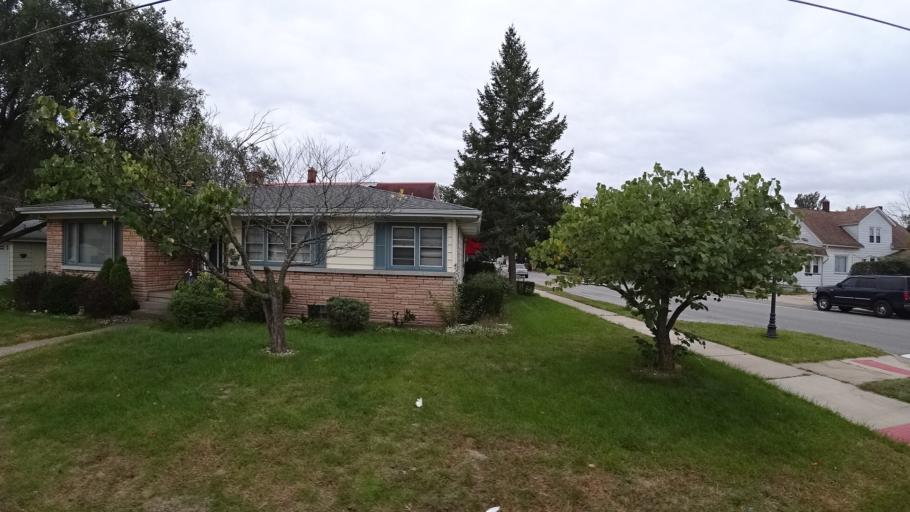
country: US
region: Indiana
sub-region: LaPorte County
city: Michigan City
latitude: 41.7025
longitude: -86.9038
